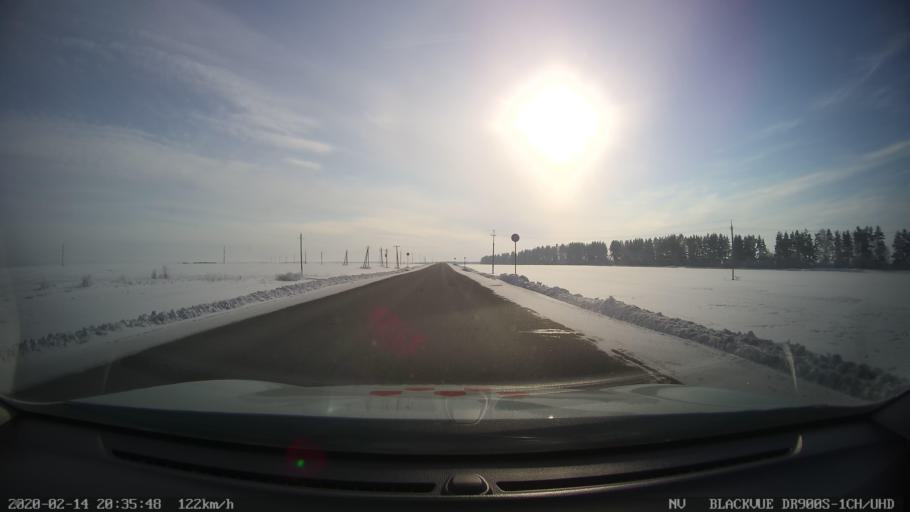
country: RU
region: Tatarstan
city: Kuybyshevskiy Zaton
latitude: 55.3773
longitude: 48.9905
